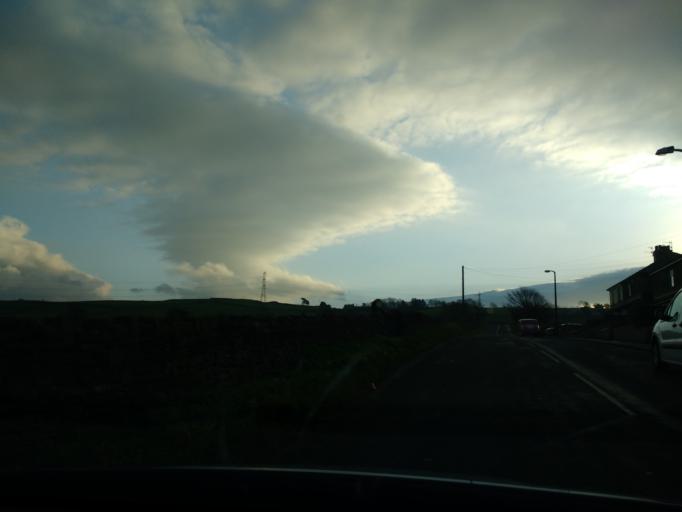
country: GB
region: England
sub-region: Lancashire
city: Lancaster
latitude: 54.0466
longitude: -2.7696
